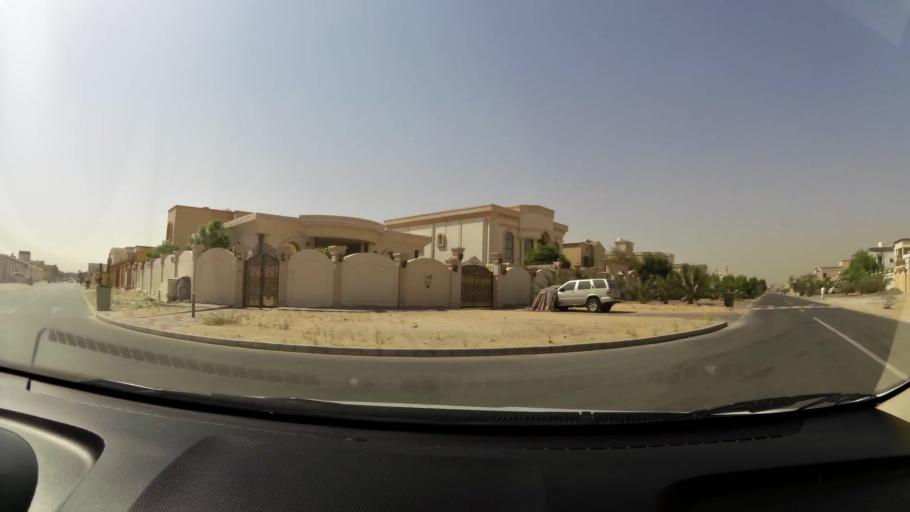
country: AE
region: Ajman
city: Ajman
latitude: 25.4140
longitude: 55.5481
